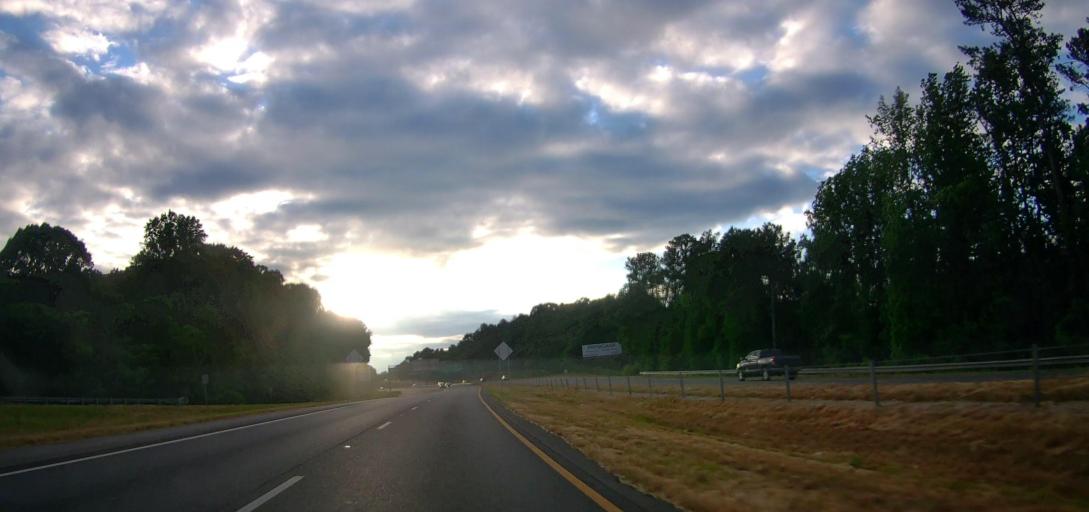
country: US
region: Georgia
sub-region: Clarke County
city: Country Club Estates
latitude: 33.9709
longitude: -83.4062
